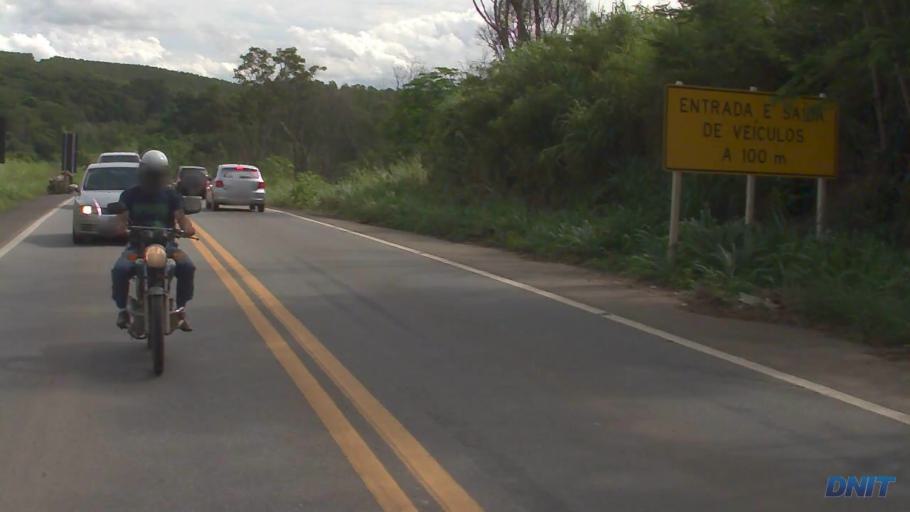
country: BR
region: Minas Gerais
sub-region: Ipaba
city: Ipaba
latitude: -19.3428
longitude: -42.4313
